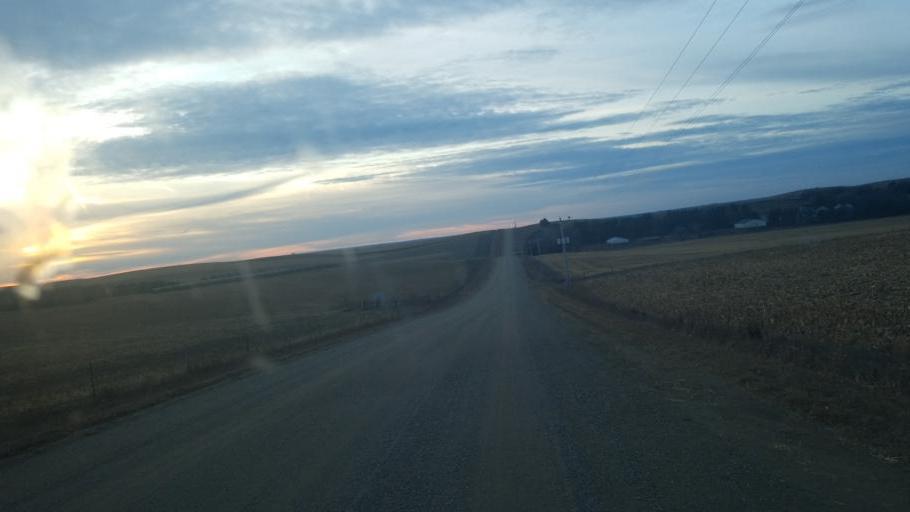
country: US
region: Nebraska
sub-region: Knox County
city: Bloomfield
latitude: 42.6845
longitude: -97.7100
